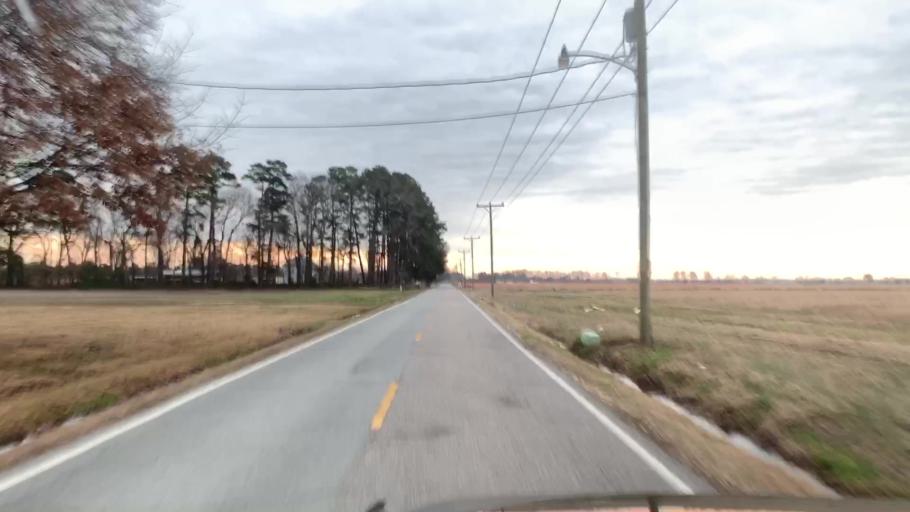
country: US
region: North Carolina
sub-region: Currituck County
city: Moyock
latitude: 36.6309
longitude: -76.1770
